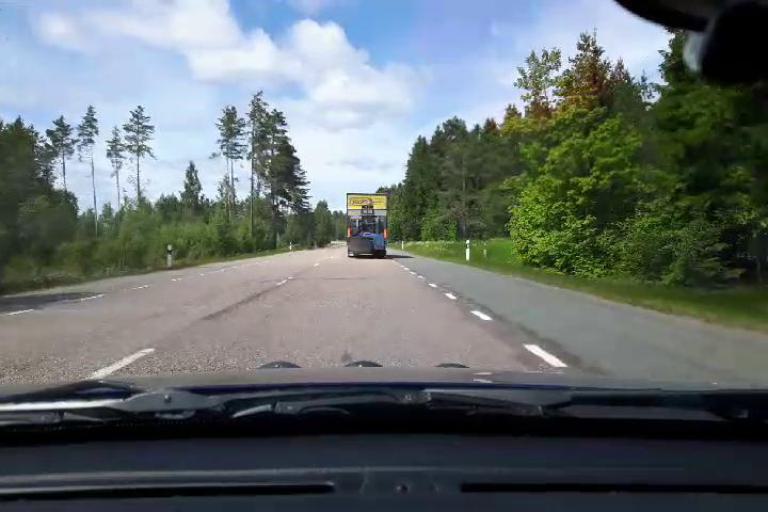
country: SE
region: Uppsala
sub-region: Osthammars Kommun
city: Bjorklinge
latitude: 60.1031
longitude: 17.5502
